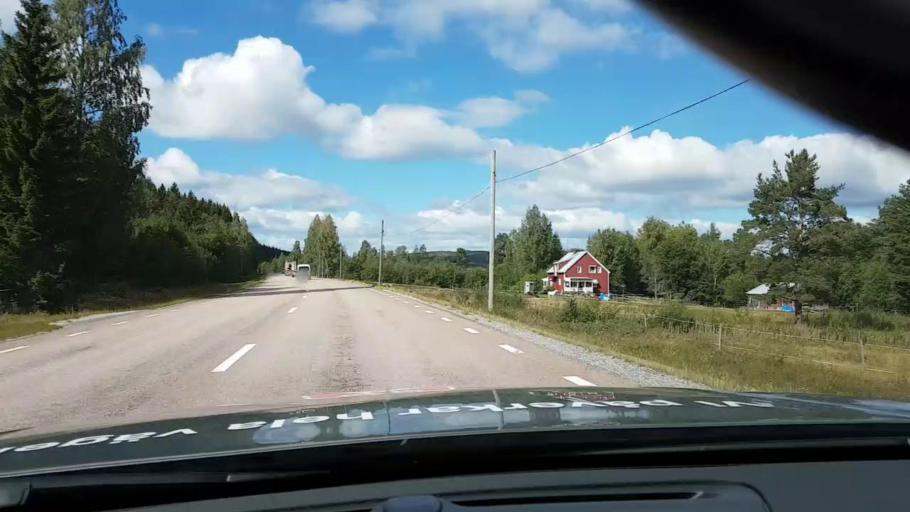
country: SE
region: Vaesternorrland
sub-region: OErnskoeldsviks Kommun
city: Bjasta
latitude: 63.3570
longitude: 18.4811
